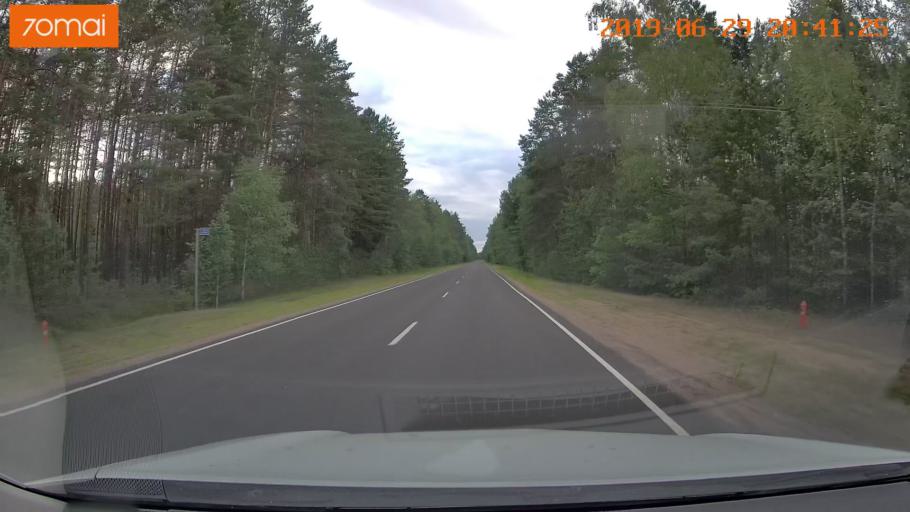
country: BY
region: Brest
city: Hantsavichy
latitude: 52.5854
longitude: 26.3398
